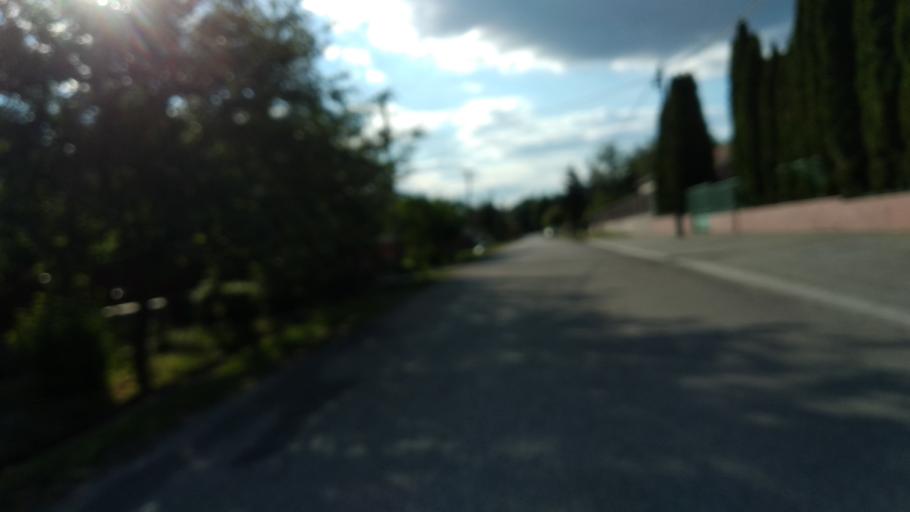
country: HU
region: Pest
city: Godollo
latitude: 47.5890
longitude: 19.3481
